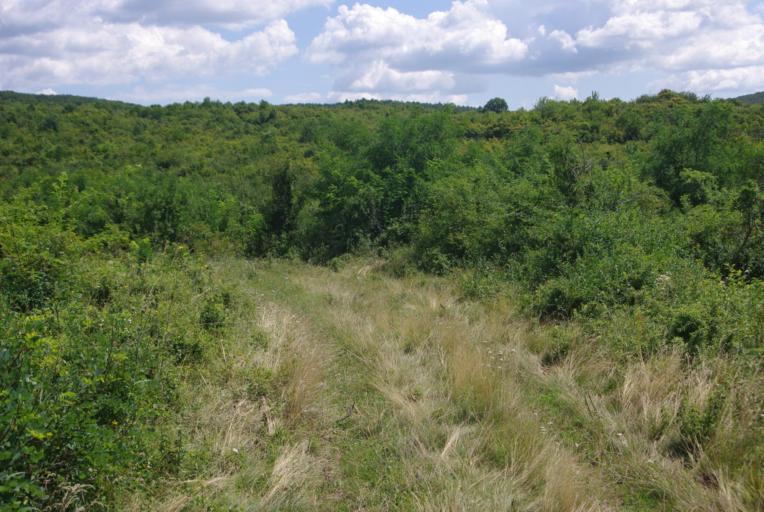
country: HU
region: Borsod-Abauj-Zemplen
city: Gonc
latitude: 48.3974
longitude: 21.2923
